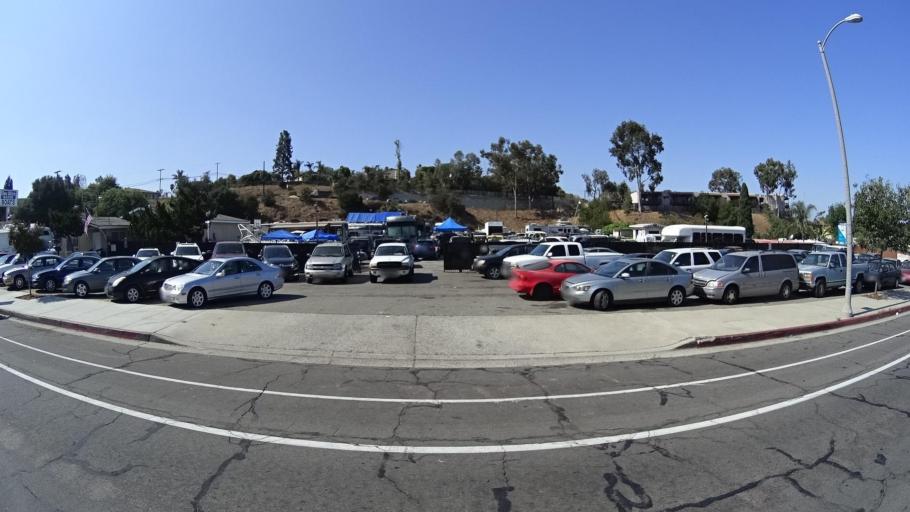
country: US
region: California
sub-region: San Diego County
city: Vista
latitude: 33.1910
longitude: -117.2282
